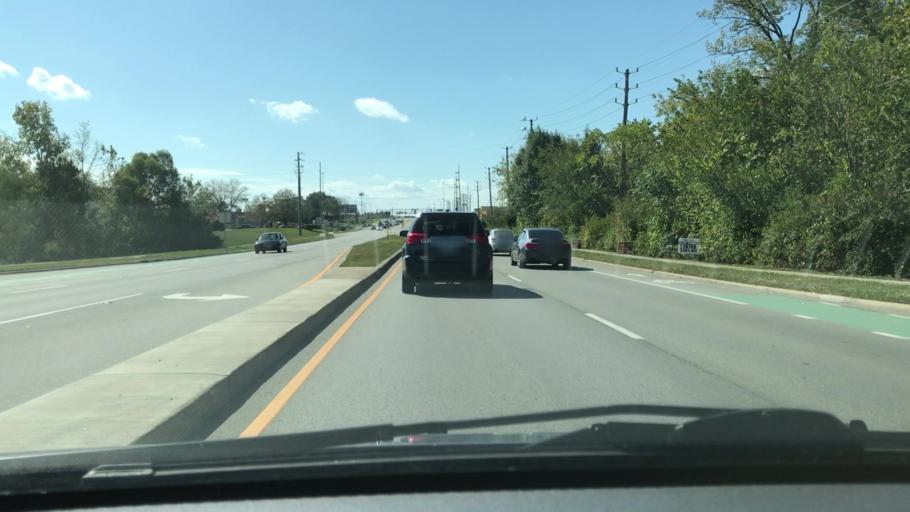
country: US
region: Indiana
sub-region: Hamilton County
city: Fishers
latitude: 39.9158
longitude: -86.0731
